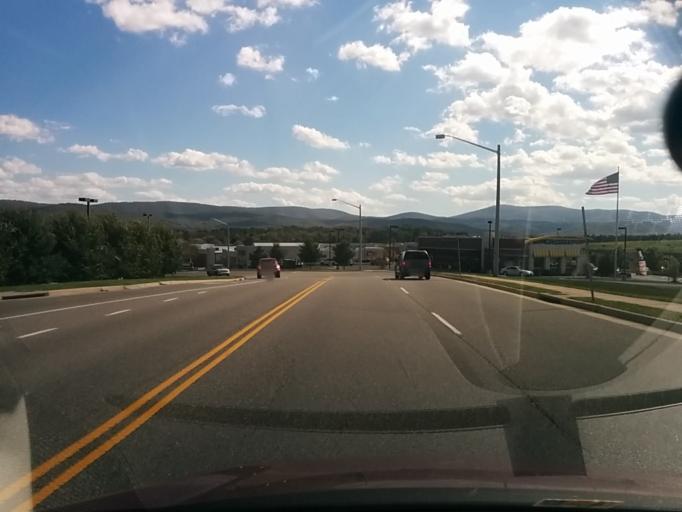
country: US
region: Virginia
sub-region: Augusta County
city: Lyndhurst
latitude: 38.0588
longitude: -78.9453
